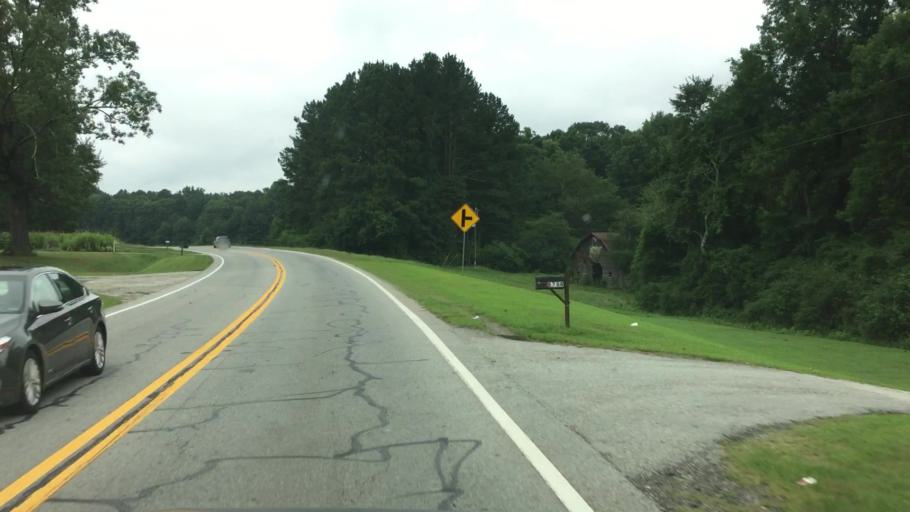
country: US
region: Georgia
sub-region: Jackson County
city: Hoschton
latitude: 34.0848
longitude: -83.8003
